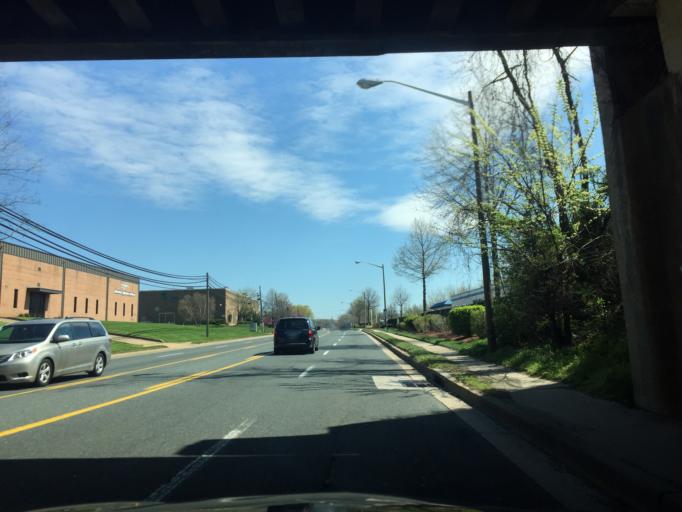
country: US
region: Maryland
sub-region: Baltimore County
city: Rossville
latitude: 39.3363
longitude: -76.4798
